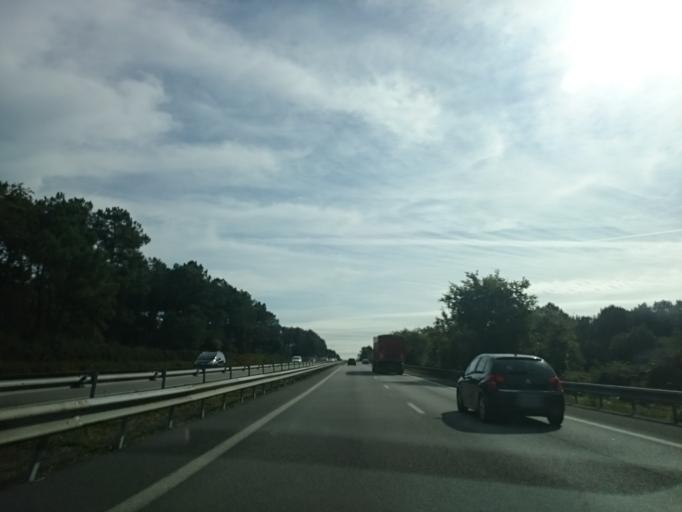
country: FR
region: Brittany
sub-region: Departement du Morbihan
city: Marzan
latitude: 47.5377
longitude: -2.3552
